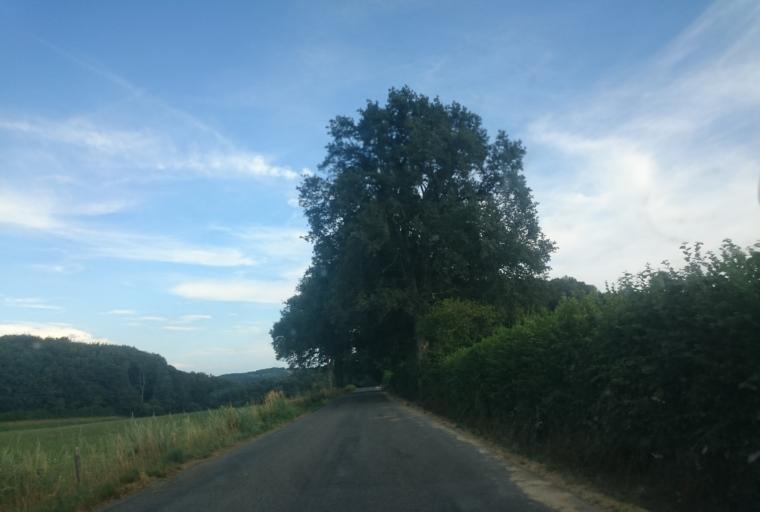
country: FR
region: Auvergne
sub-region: Departement du Cantal
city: Laroquebrou
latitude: 44.9328
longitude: 2.1930
